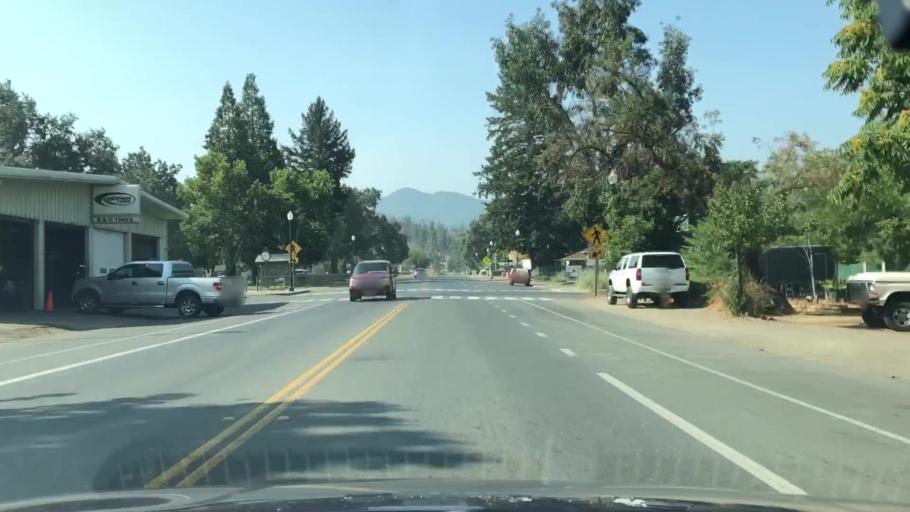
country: US
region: California
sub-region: Lake County
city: Middletown
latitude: 38.7512
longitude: -122.6157
